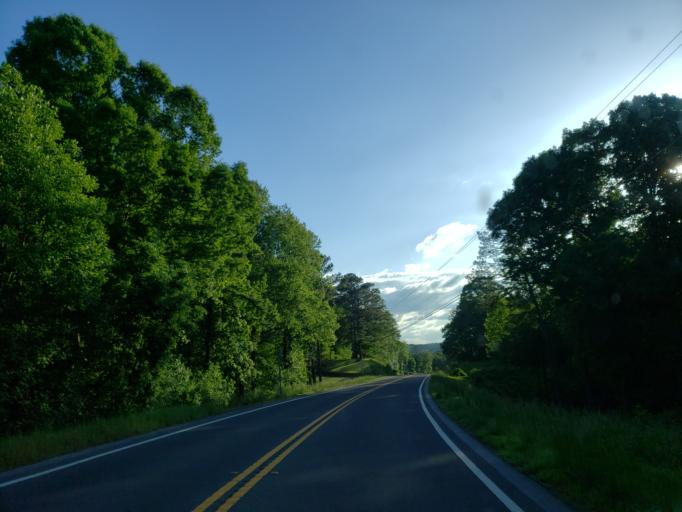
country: US
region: Georgia
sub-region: Cherokee County
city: Canton
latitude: 34.2647
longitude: -84.5868
